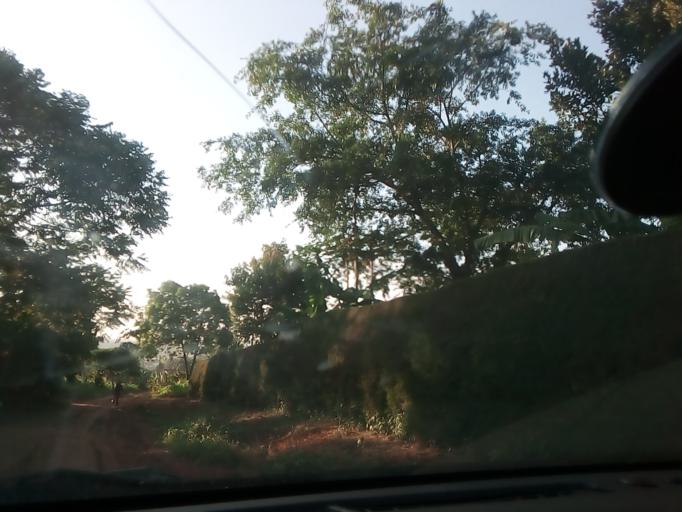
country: UG
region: Central Region
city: Masaka
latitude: -0.3408
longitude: 31.7578
